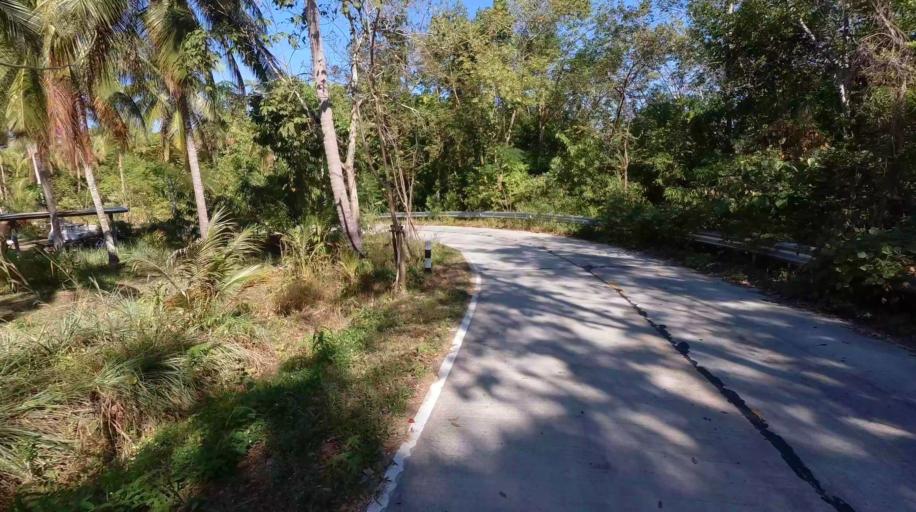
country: TH
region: Trat
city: Ko Kut
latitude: 11.6152
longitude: 102.5422
